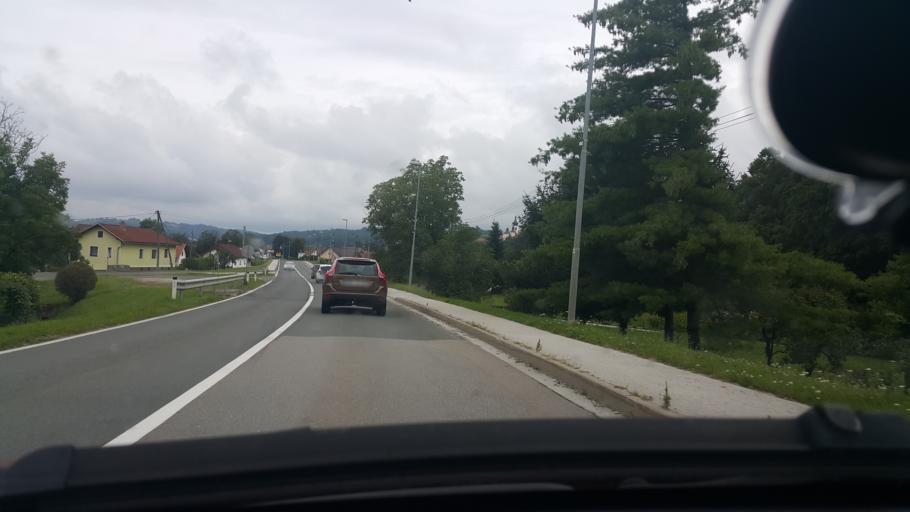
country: SI
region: Ormoz
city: Ormoz
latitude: 46.4126
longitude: 16.1176
